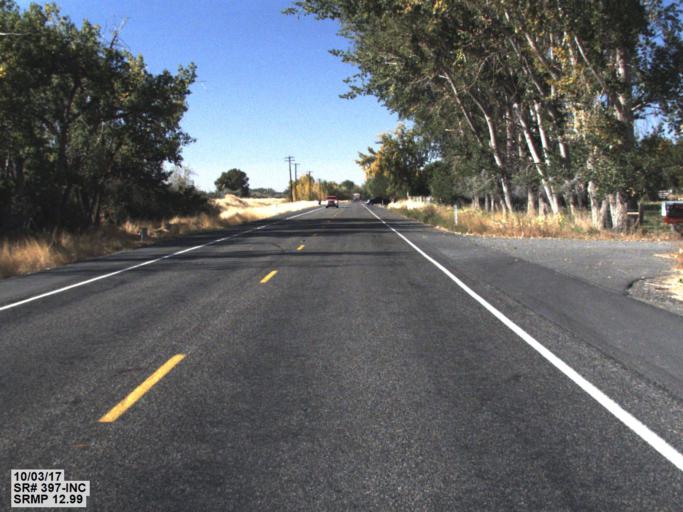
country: US
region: Washington
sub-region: Benton County
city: Finley
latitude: 46.1633
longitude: -119.0434
